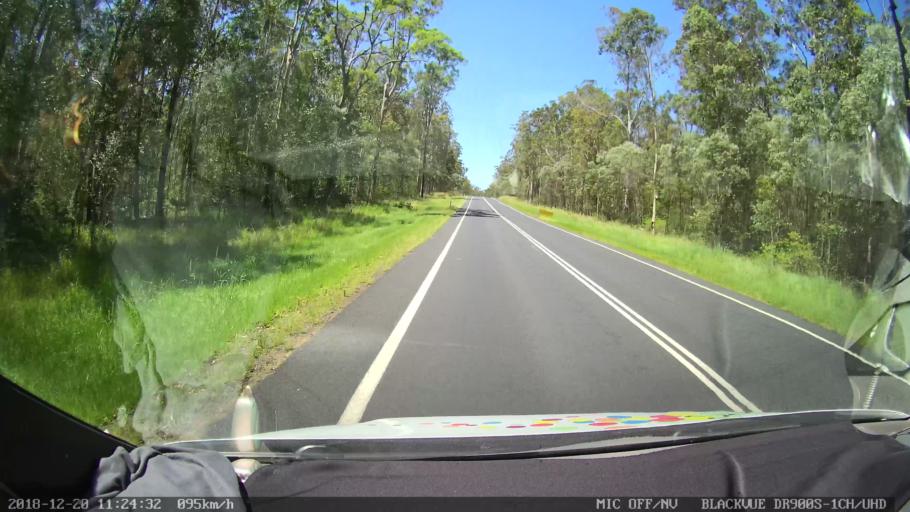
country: AU
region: New South Wales
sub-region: Richmond Valley
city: Casino
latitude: -29.0754
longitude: 153.0016
